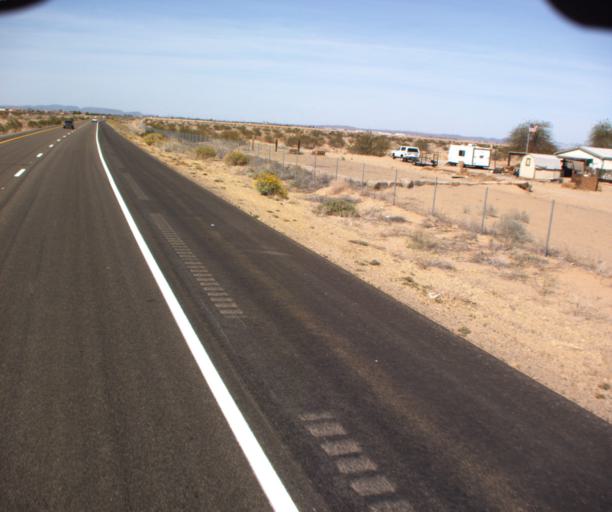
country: US
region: Arizona
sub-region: Yuma County
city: Fortuna Foothills
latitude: 32.6330
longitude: -114.5209
